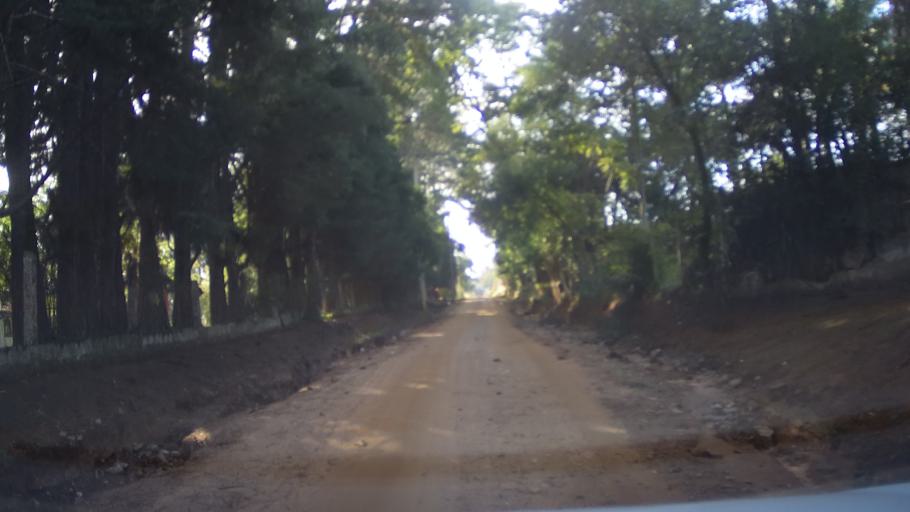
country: BR
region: Sao Paulo
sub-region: Itupeva
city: Itupeva
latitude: -23.2169
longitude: -47.0672
